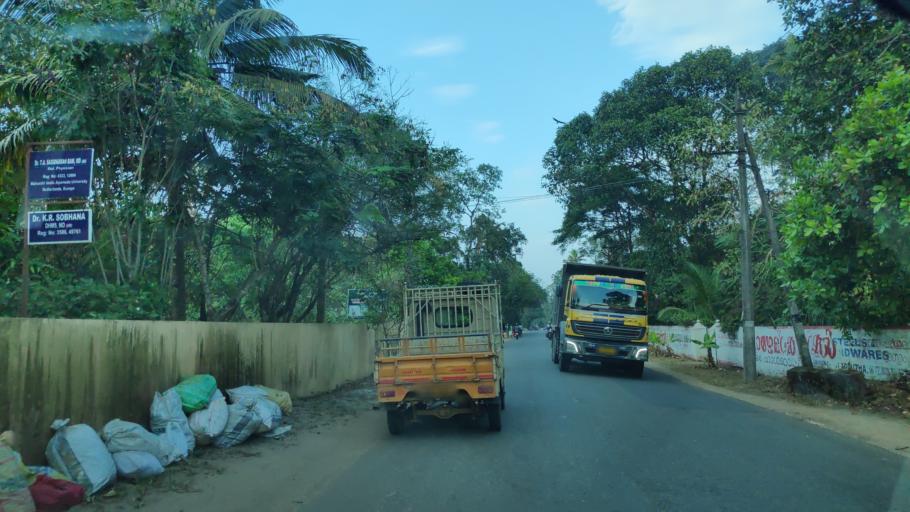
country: IN
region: Kerala
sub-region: Alappuzha
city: Shertallai
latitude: 9.6437
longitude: 76.3701
